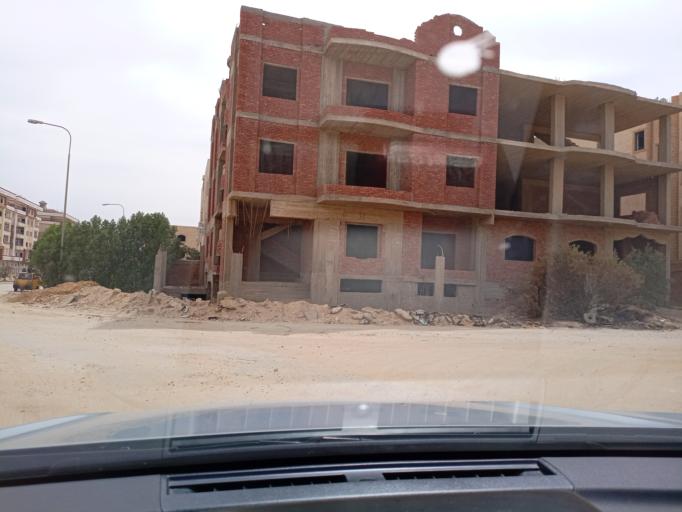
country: EG
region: Muhafazat al Qalyubiyah
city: Al Khankah
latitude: 30.2491
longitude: 31.5014
